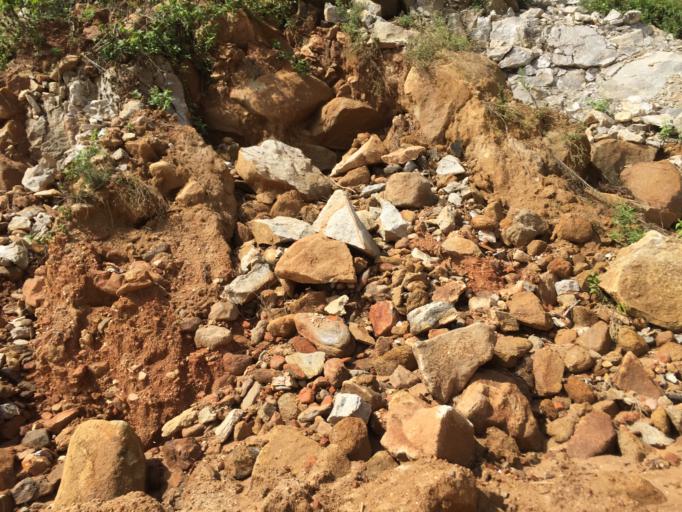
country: VN
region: Quang Nam
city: Hoi An
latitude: 15.9685
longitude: 108.5079
